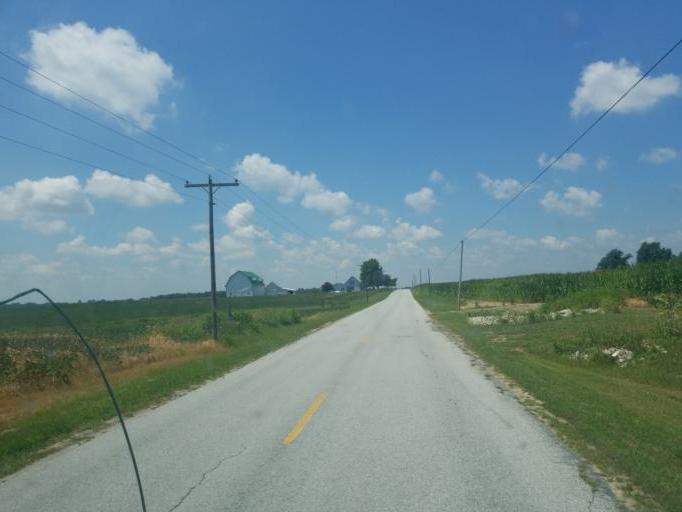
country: US
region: Ohio
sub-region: Allen County
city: Spencerville
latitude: 40.6776
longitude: -84.4395
